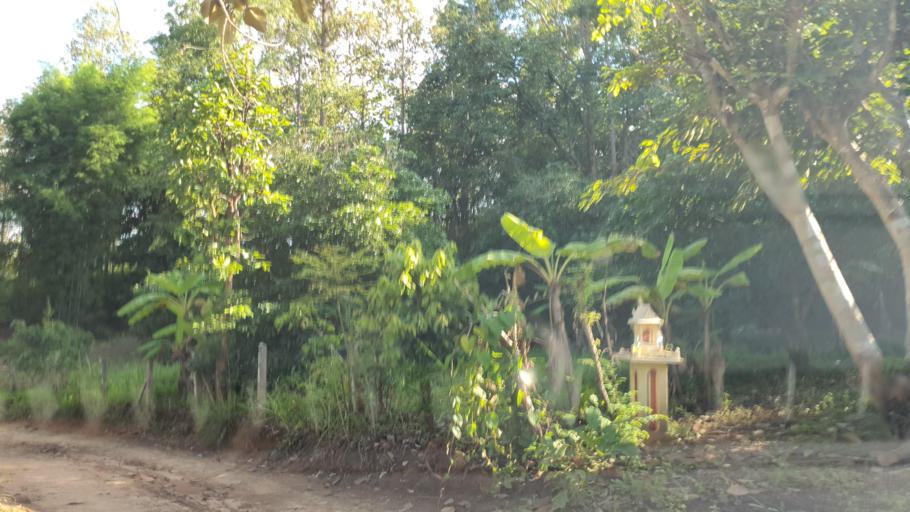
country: TH
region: Chiang Mai
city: Hang Dong
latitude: 18.7240
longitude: 98.8491
